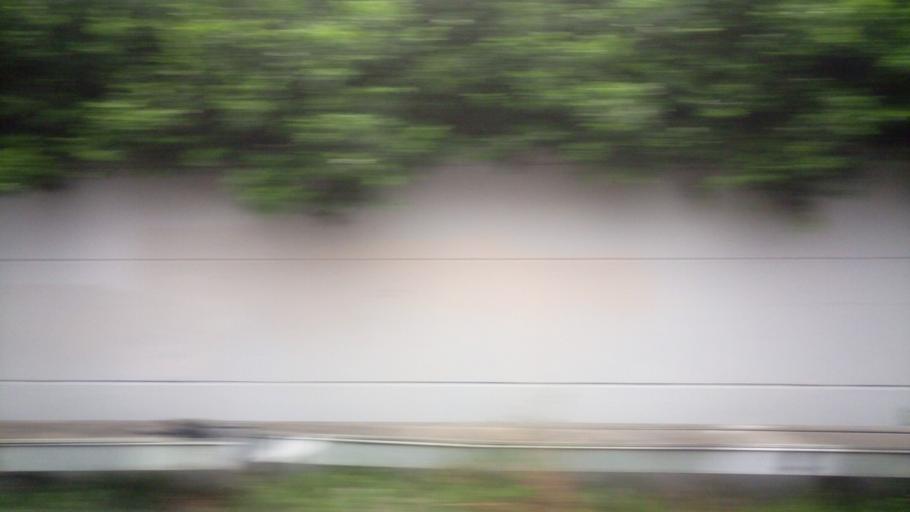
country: AU
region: New South Wales
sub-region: Strathfield
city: Homebush
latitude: -33.8733
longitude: 151.0966
